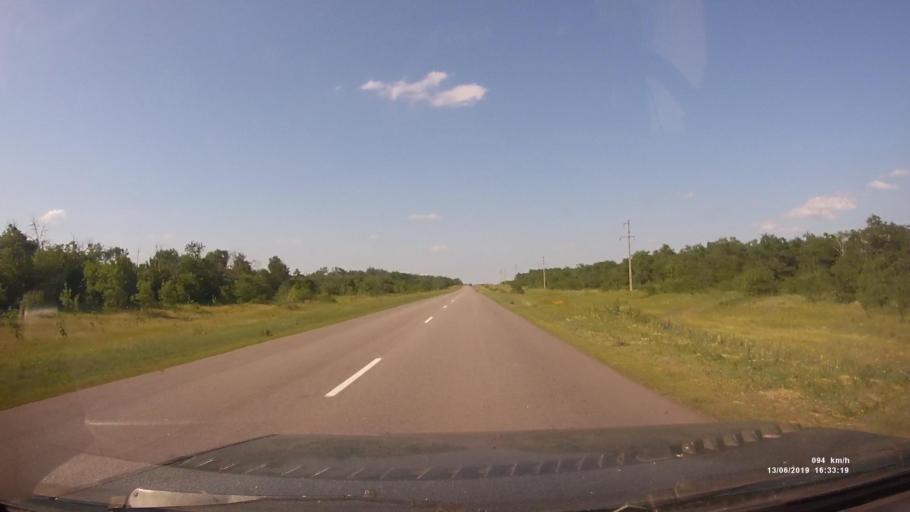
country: RU
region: Rostov
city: Kazanskaya
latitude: 49.8591
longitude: 41.2791
